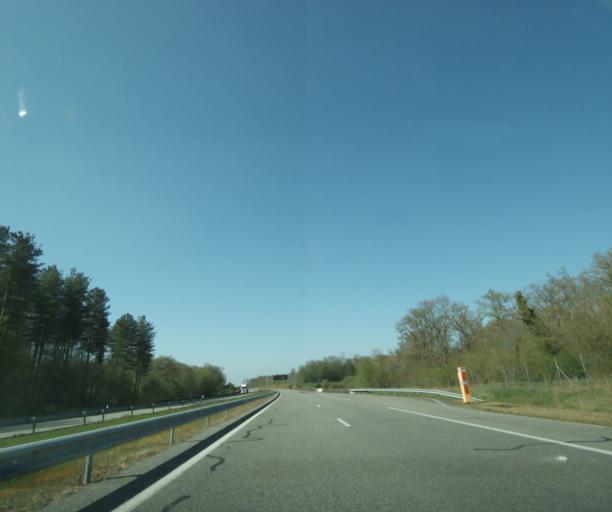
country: FR
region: Centre
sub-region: Departement du Loiret
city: Ouzouer-sur-Trezee
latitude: 47.7334
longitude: 2.7358
